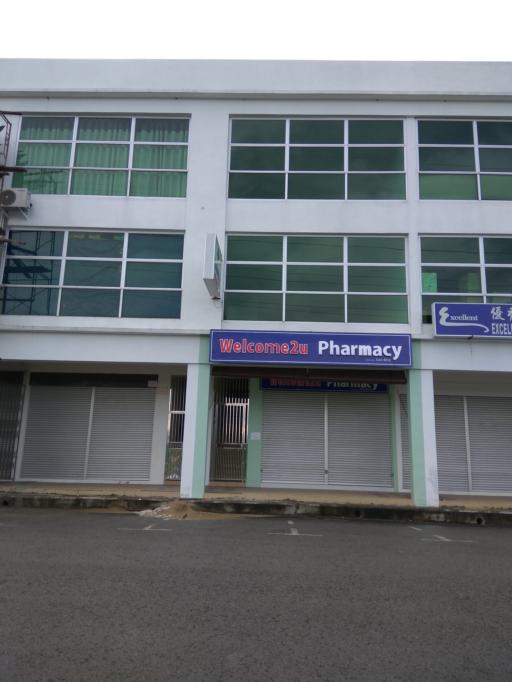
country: MY
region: Sarawak
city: Sibu
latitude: 2.2744
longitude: 111.8731
